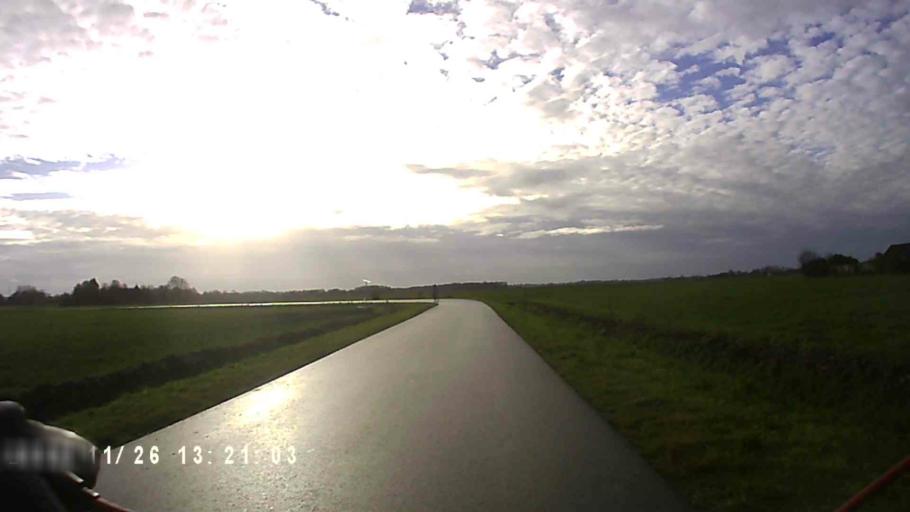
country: NL
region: Groningen
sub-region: Gemeente Delfzijl
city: Delfzijl
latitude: 53.3493
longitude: 6.8915
